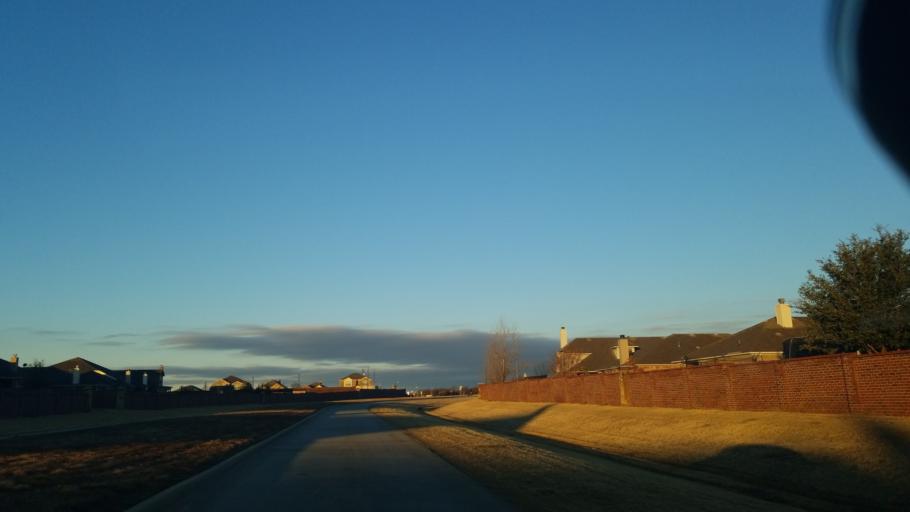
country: US
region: Texas
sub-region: Denton County
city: Argyle
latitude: 33.1699
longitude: -97.1636
